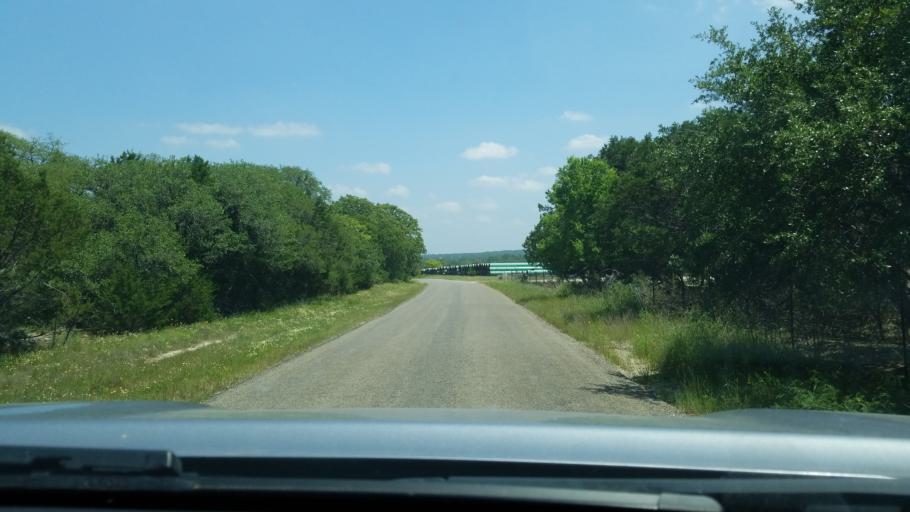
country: US
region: Texas
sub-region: Blanco County
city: Blanco
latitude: 30.0774
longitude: -98.3995
